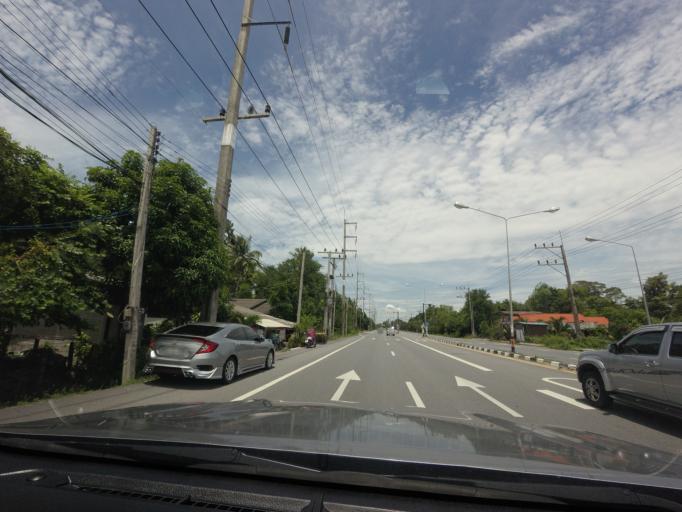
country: TH
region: Songkhla
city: Krasae Sin
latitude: 7.5844
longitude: 100.4062
